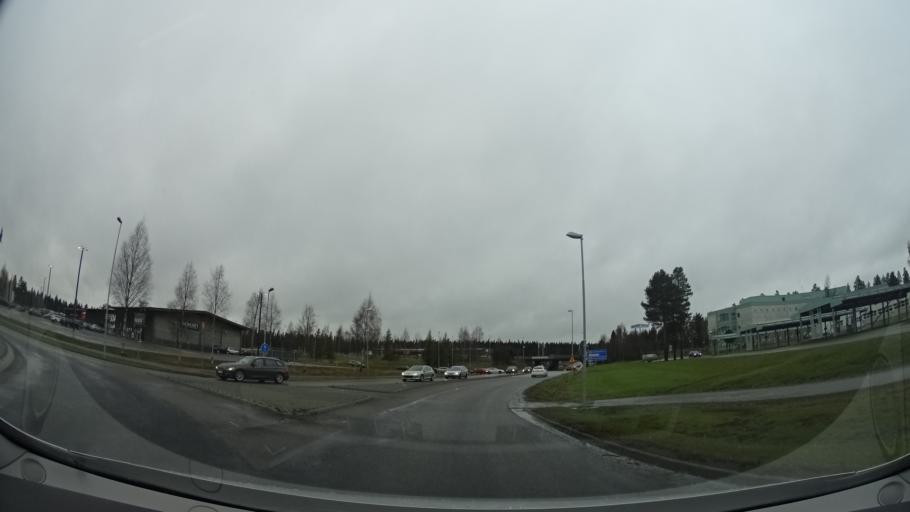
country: SE
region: Vaesterbotten
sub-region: Skelleftea Kommun
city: Skelleftea
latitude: 64.7680
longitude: 21.0218
